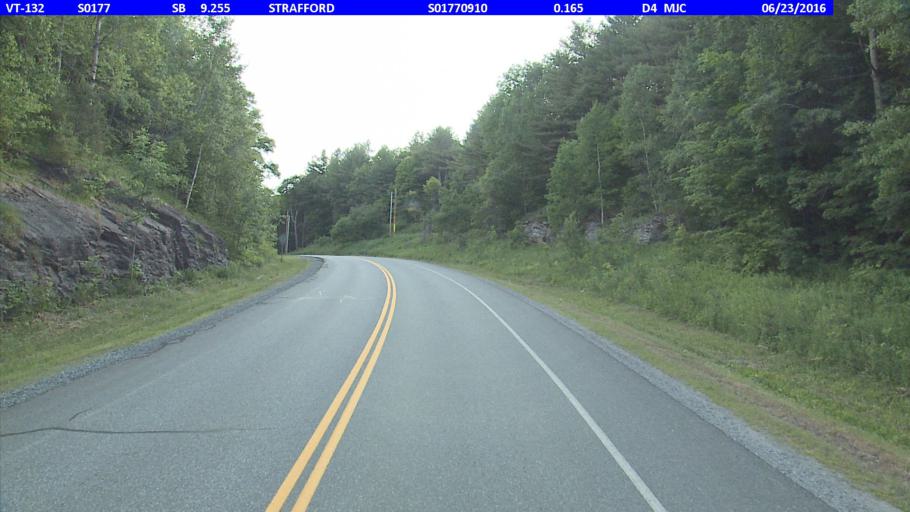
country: US
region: New Hampshire
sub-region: Grafton County
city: Hanover
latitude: 43.8271
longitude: -72.4017
